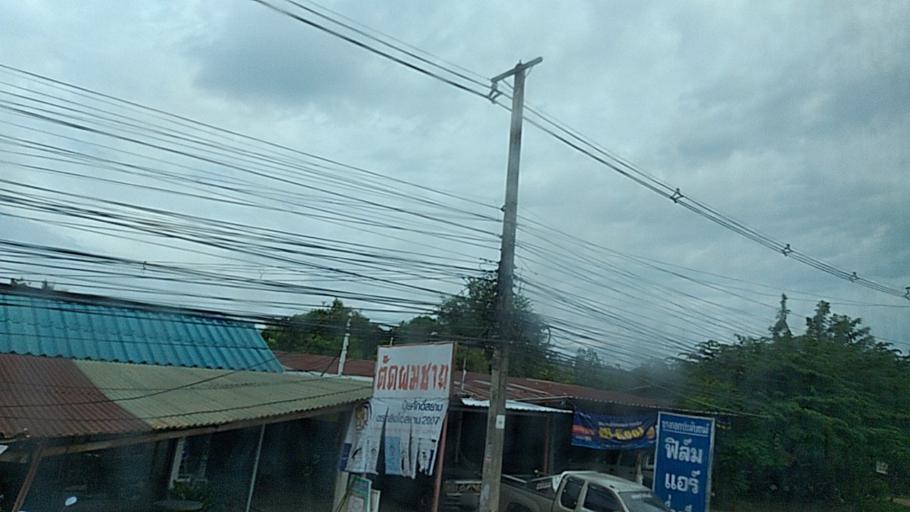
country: TH
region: Maha Sarakham
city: Maha Sarakham
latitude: 16.1670
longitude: 103.3282
